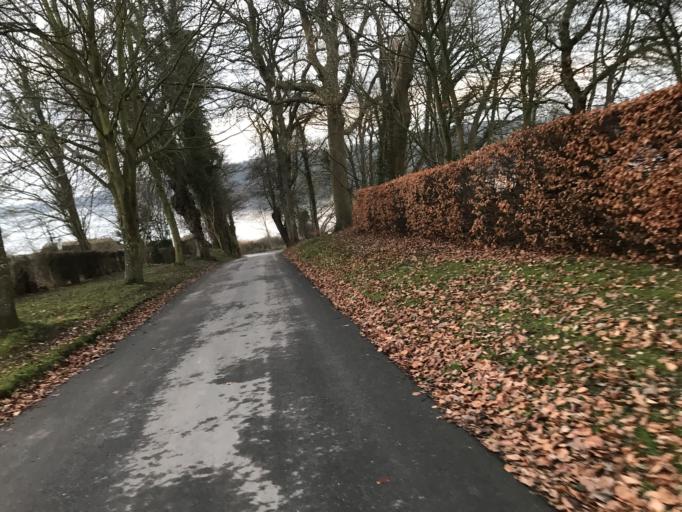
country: DK
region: South Denmark
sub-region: Fredericia Kommune
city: Snoghoj
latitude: 55.5038
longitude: 9.6904
